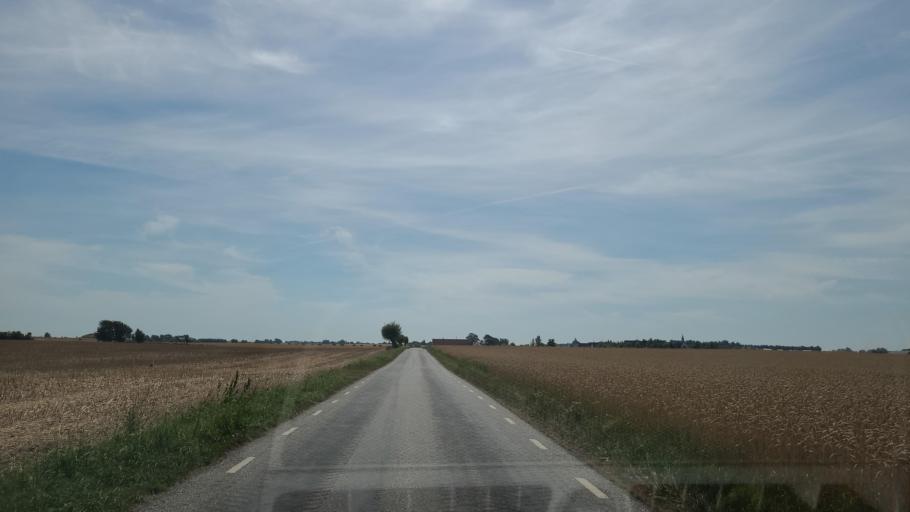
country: SE
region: Skane
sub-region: Malmo
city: Oxie
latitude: 55.4650
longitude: 13.0951
